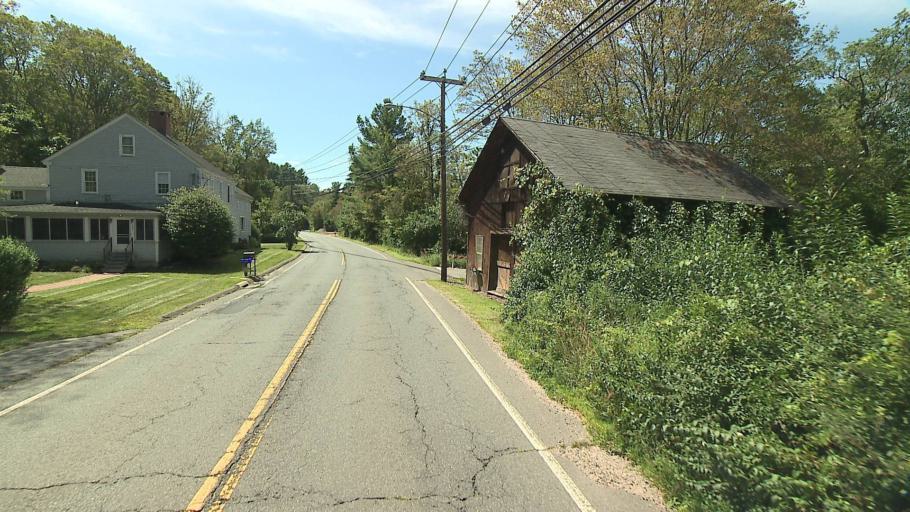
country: US
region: Connecticut
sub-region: Hartford County
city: Canton Valley
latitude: 41.8645
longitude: -72.9051
